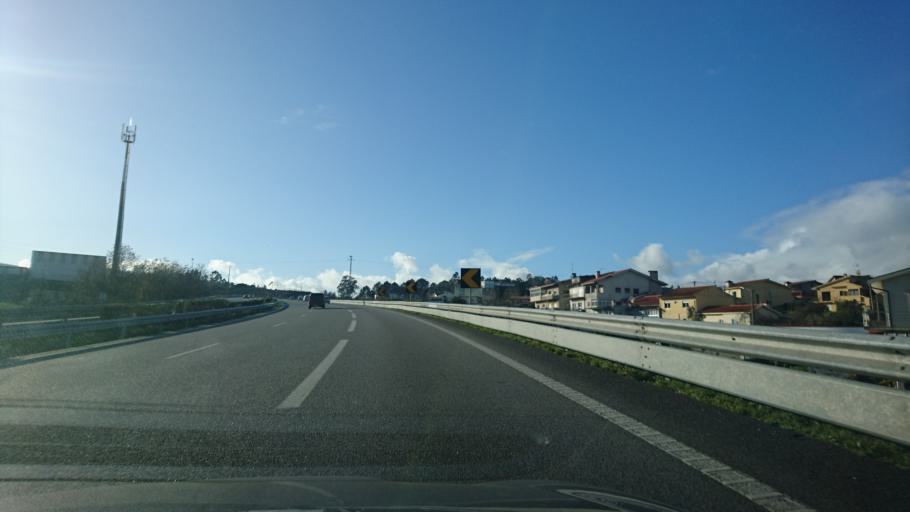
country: PT
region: Porto
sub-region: Valongo
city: Campo
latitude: 41.1862
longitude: -8.4652
